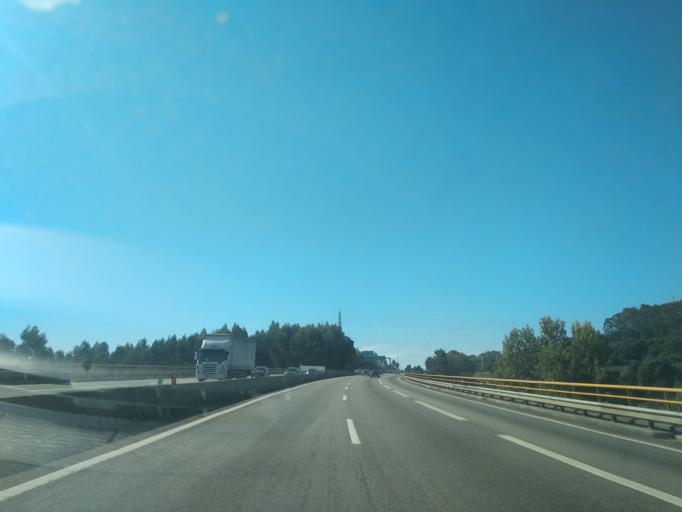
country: PT
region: Porto
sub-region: Vila Nova de Gaia
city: Perozinho
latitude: 41.0803
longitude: -8.5760
